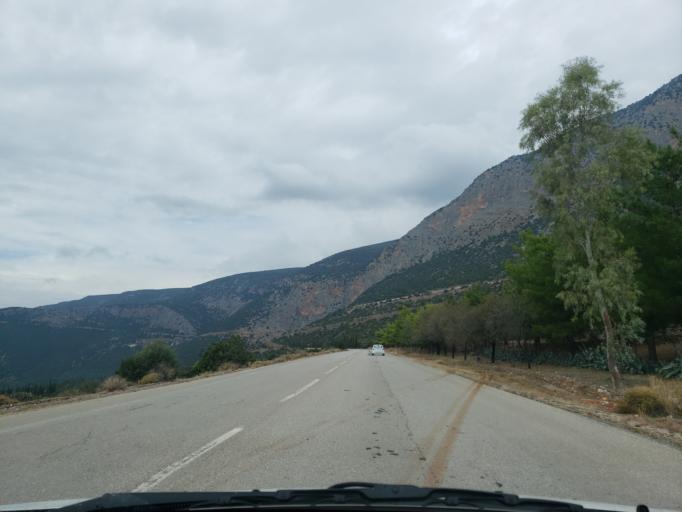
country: GR
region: Central Greece
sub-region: Nomos Fokidos
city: Delphi
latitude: 38.4845
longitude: 22.4609
